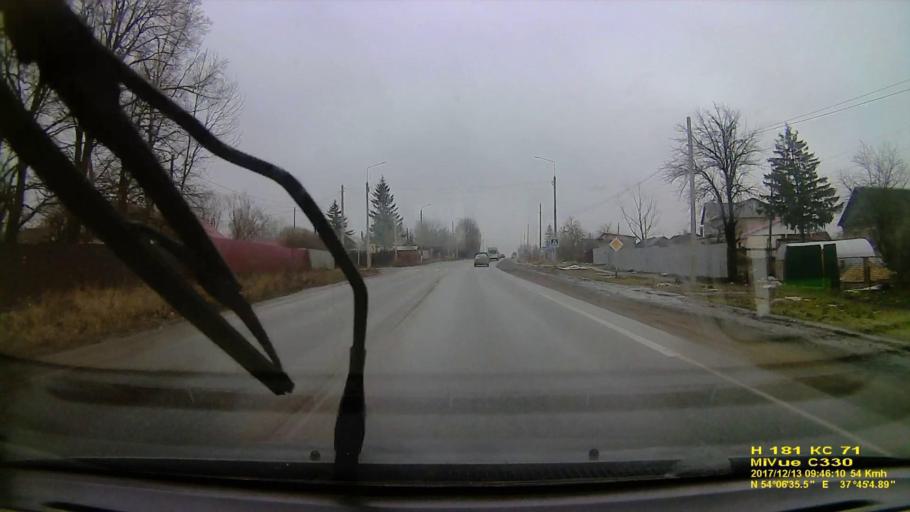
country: RU
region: Tula
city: Bolokhovo
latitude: 54.1098
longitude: 37.7515
